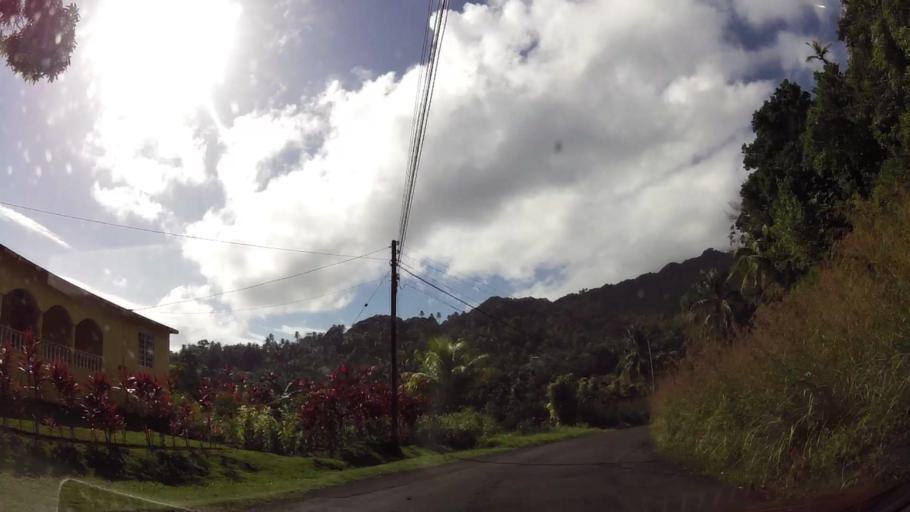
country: DM
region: Saint David
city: Castle Bruce
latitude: 15.4866
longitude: -61.2546
